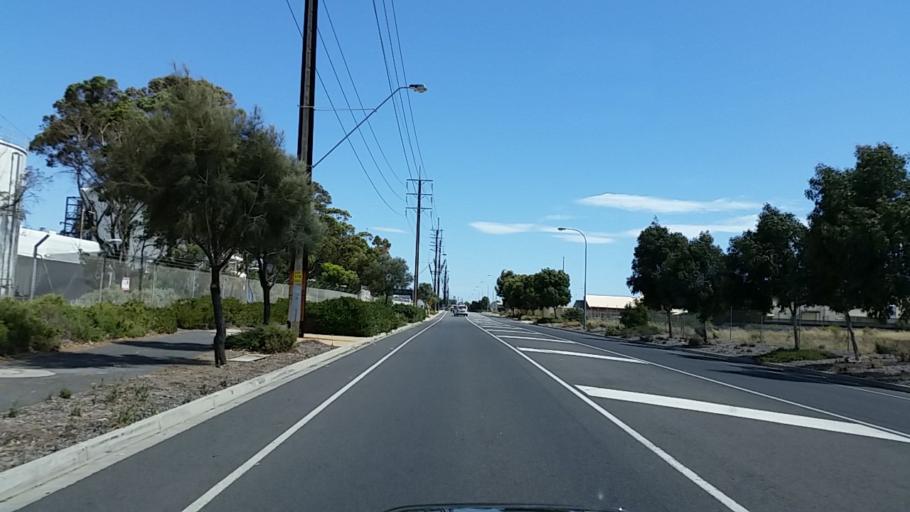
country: AU
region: South Australia
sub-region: Port Adelaide Enfield
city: Birkenhead
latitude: -34.7825
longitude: 138.5079
